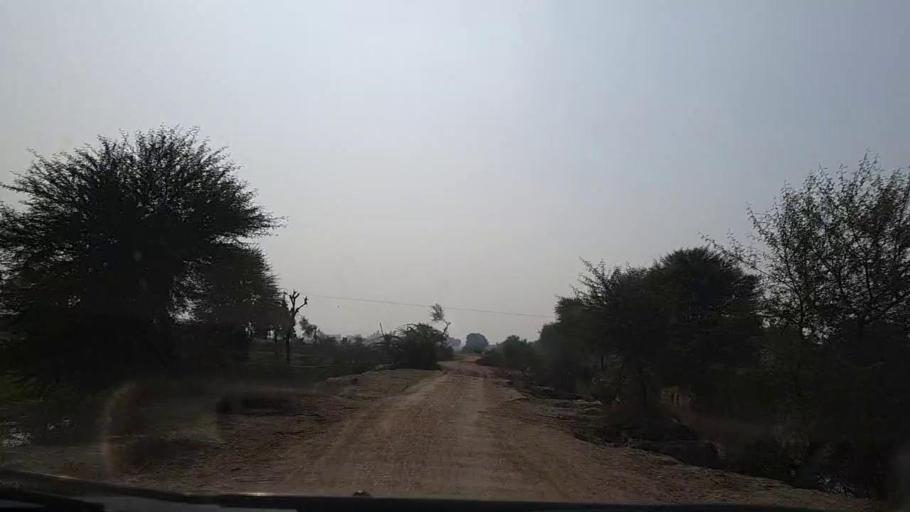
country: PK
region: Sindh
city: Sanghar
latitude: 26.0322
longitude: 68.9757
